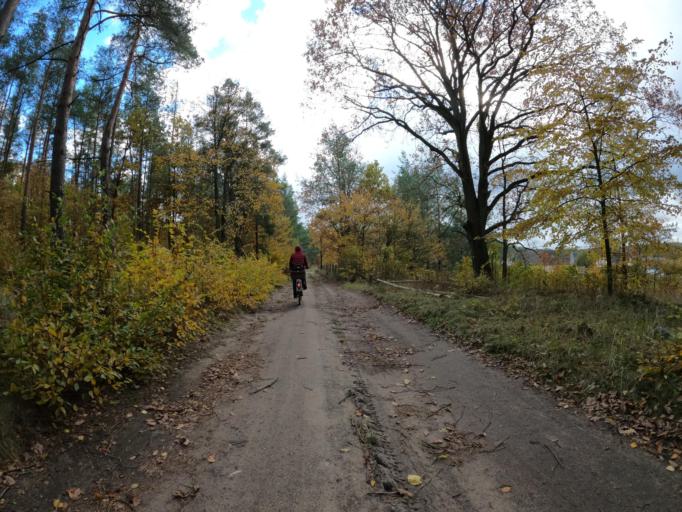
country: PL
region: West Pomeranian Voivodeship
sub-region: Powiat mysliborski
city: Barlinek
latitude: 52.9207
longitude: 15.2911
